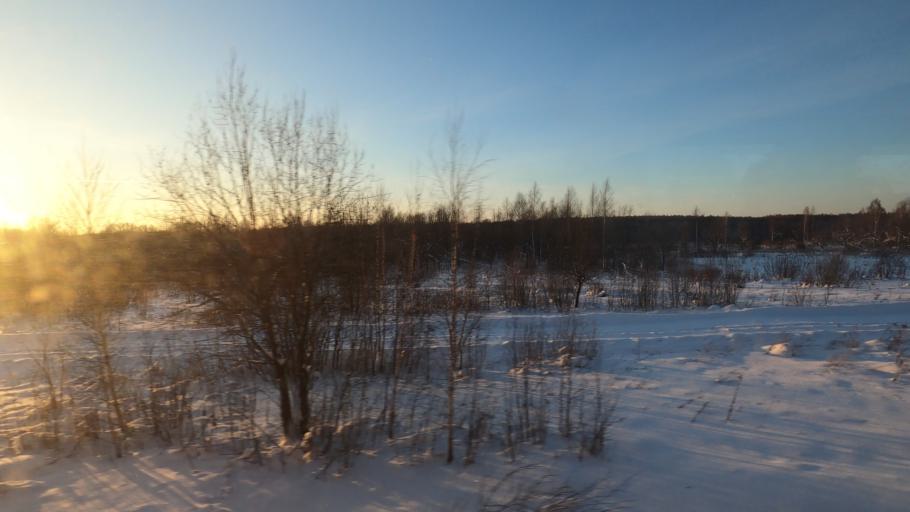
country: RU
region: Moskovskaya
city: Orud'yevo
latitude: 56.4210
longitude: 37.4976
